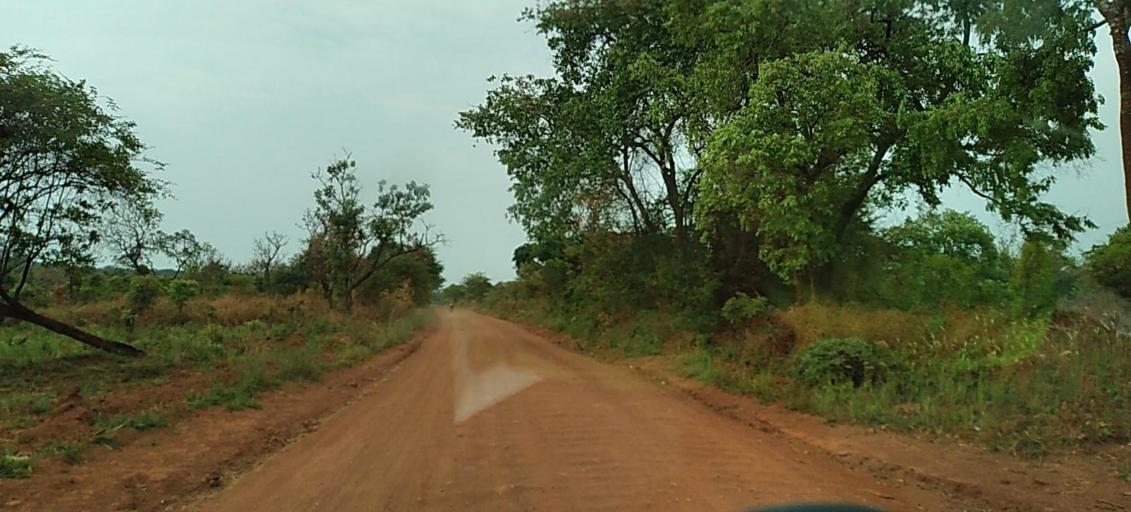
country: ZM
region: North-Western
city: Solwezi
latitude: -12.2268
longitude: 26.5105
